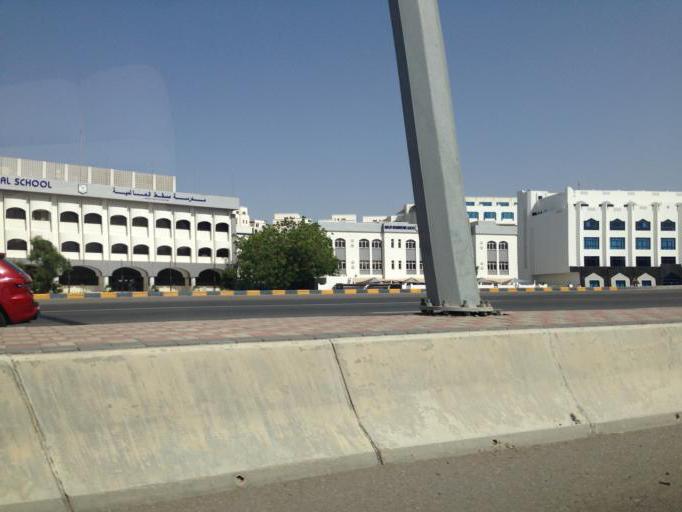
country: OM
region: Muhafazat Masqat
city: Muscat
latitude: 23.6067
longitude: 58.4907
